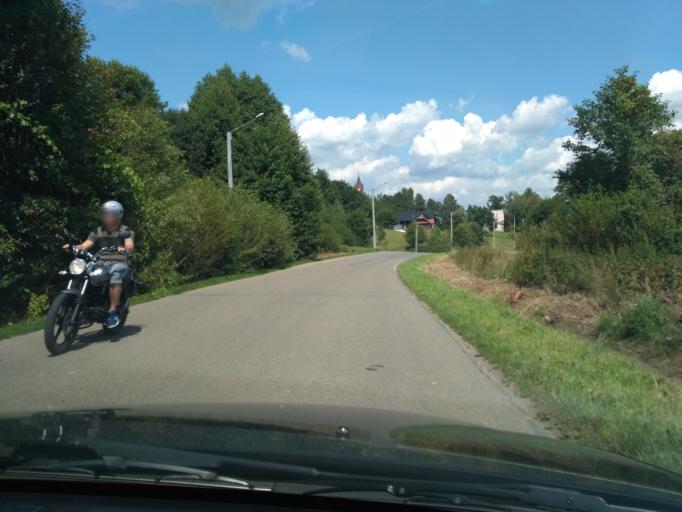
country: PL
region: Subcarpathian Voivodeship
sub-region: Powiat strzyzowski
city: Wysoka Strzyzowska
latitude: 49.8293
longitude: 21.7392
